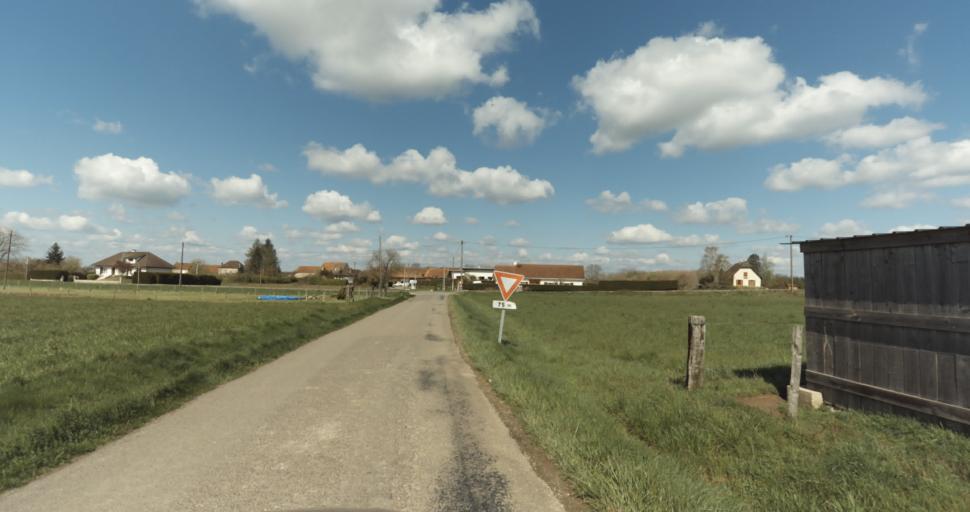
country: FR
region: Bourgogne
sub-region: Departement de la Cote-d'Or
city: Auxonne
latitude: 47.2088
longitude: 5.4157
